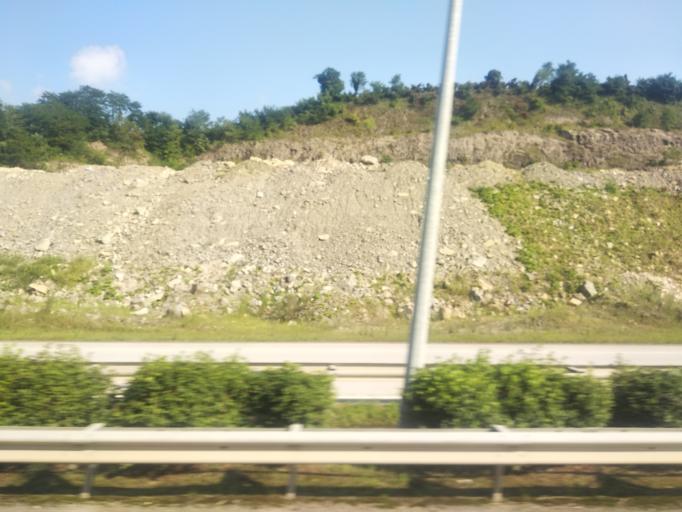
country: TR
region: Ordu
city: Ordu
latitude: 40.9982
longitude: 37.8208
